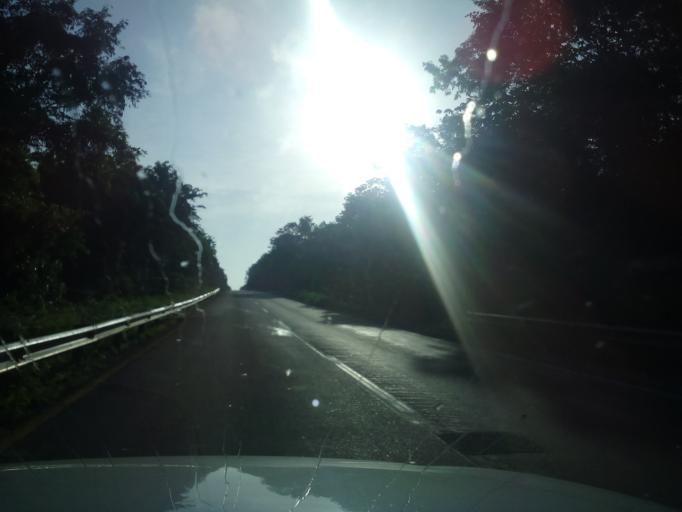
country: MX
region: Yucatan
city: Piste
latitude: 20.7439
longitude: -88.6823
